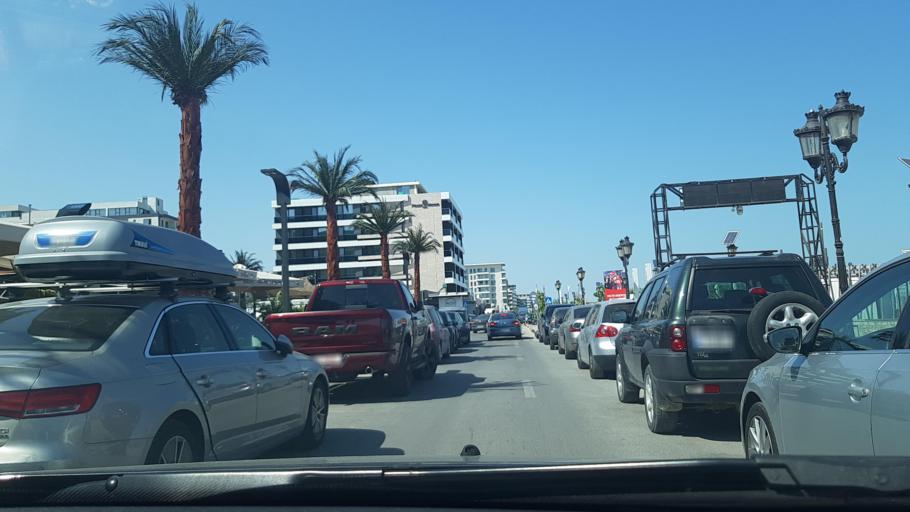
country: RO
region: Constanta
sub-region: Comuna Navodari
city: Navodari
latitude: 44.3017
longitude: 28.6266
